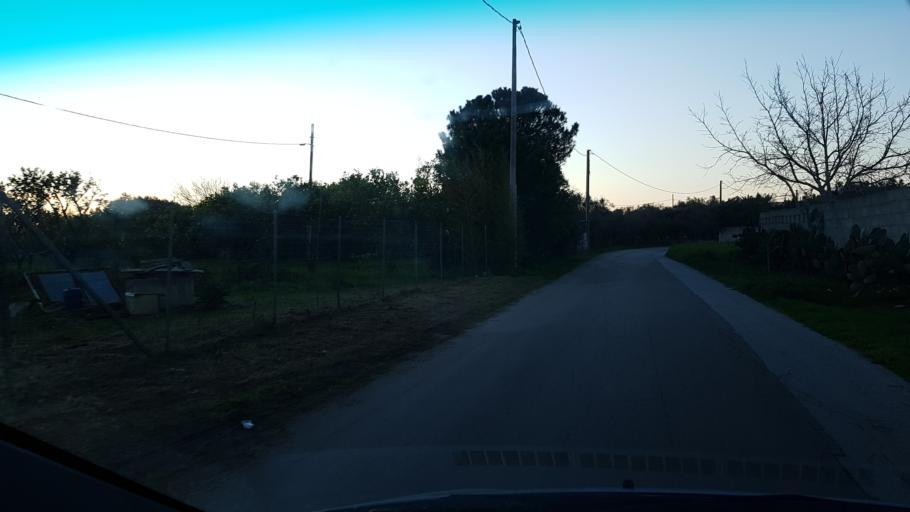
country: IT
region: Apulia
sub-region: Provincia di Brindisi
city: San Pietro Vernotico
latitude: 40.4966
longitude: 17.9877
